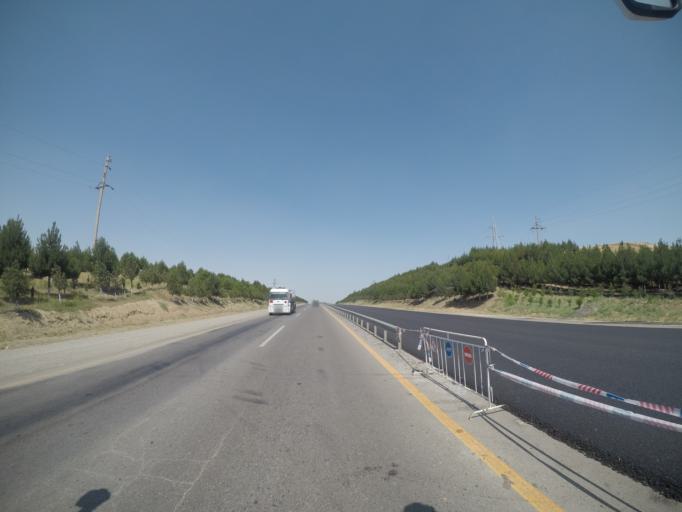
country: AZ
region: Haciqabul
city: Haciqabul
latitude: 40.0455
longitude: 48.9766
